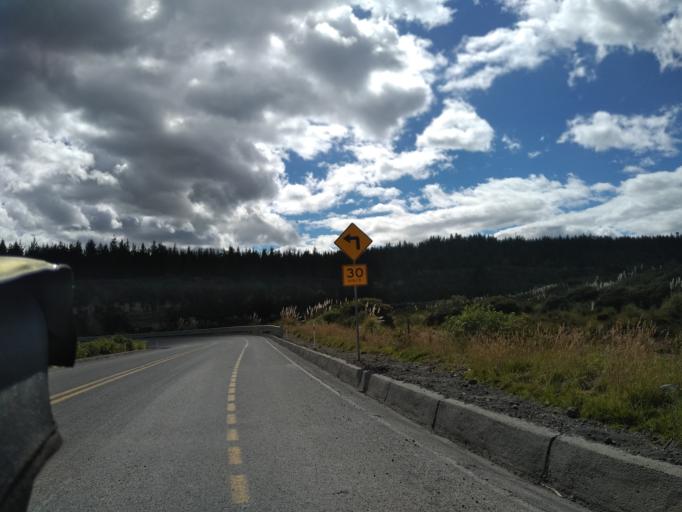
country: EC
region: Cotopaxi
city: Saquisili
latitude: -0.6921
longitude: -78.5677
